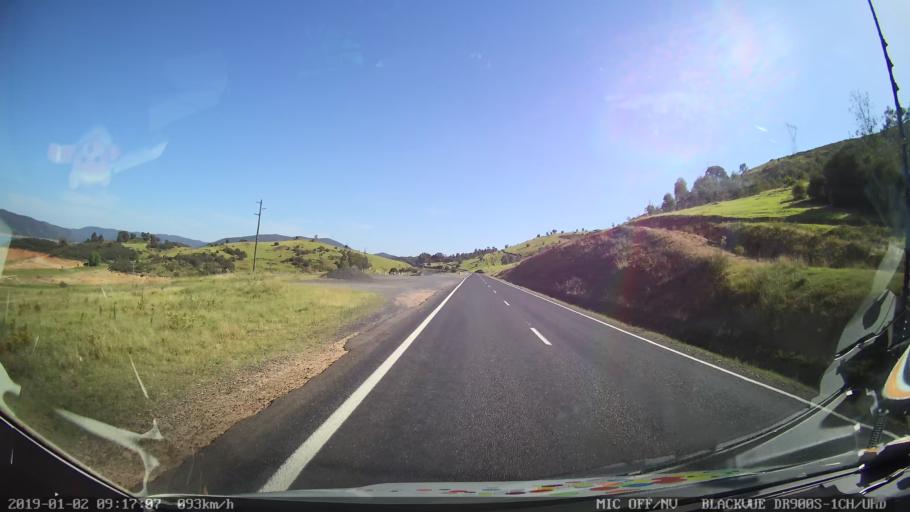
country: AU
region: New South Wales
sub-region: Tumut Shire
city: Tumut
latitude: -35.4455
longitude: 148.2866
